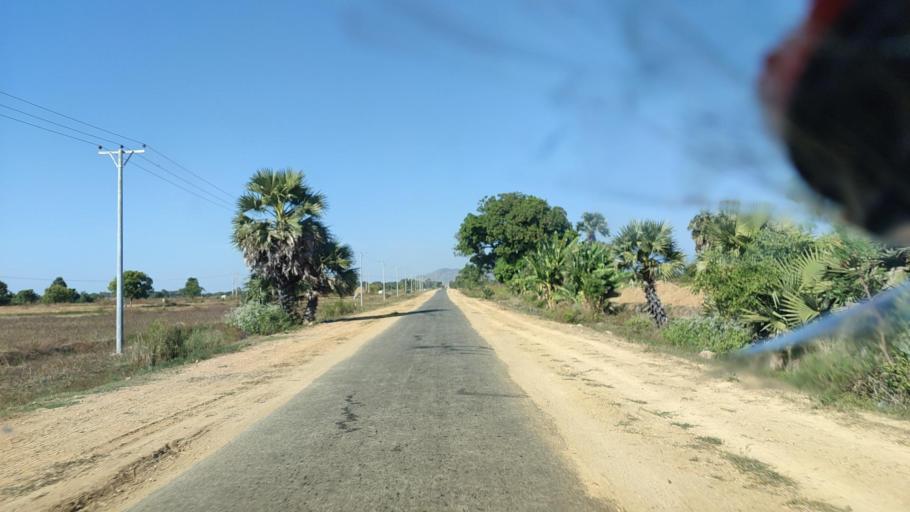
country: MM
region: Mandalay
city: Yamethin
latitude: 20.1775
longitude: 96.2620
